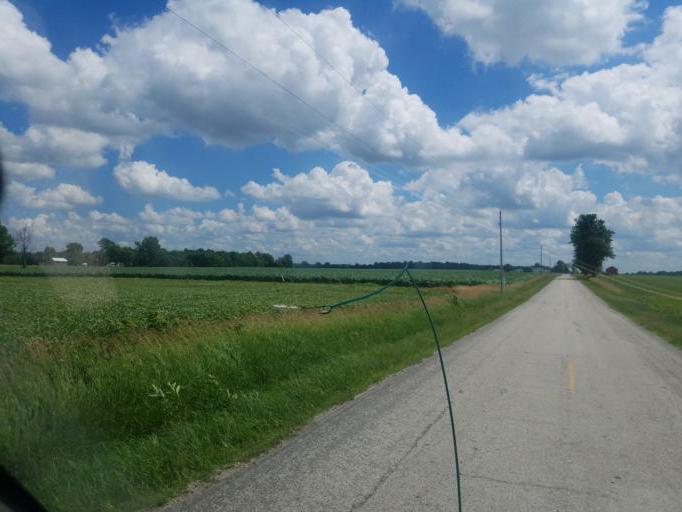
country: US
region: Ohio
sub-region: Crawford County
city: Crestline
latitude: 40.9004
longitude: -82.8264
